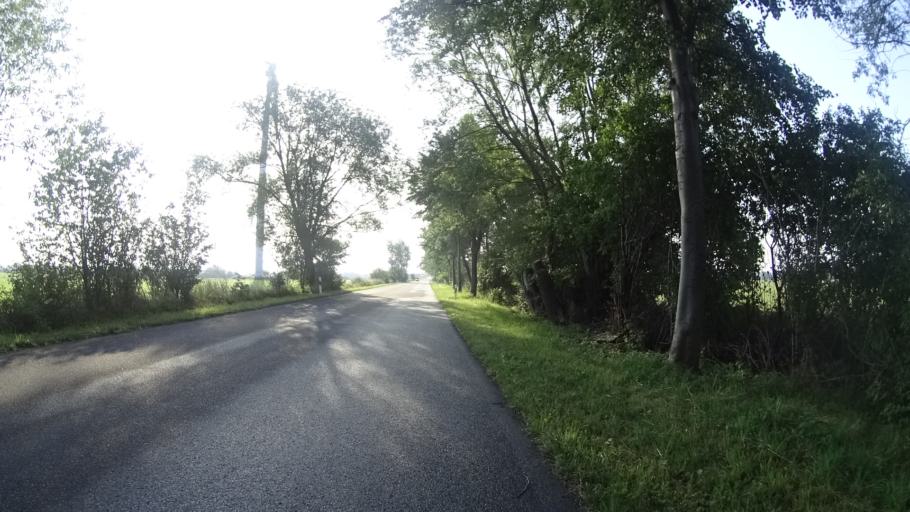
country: DE
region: Brandenburg
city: Kasel-Golzig
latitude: 51.9815
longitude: 13.7318
